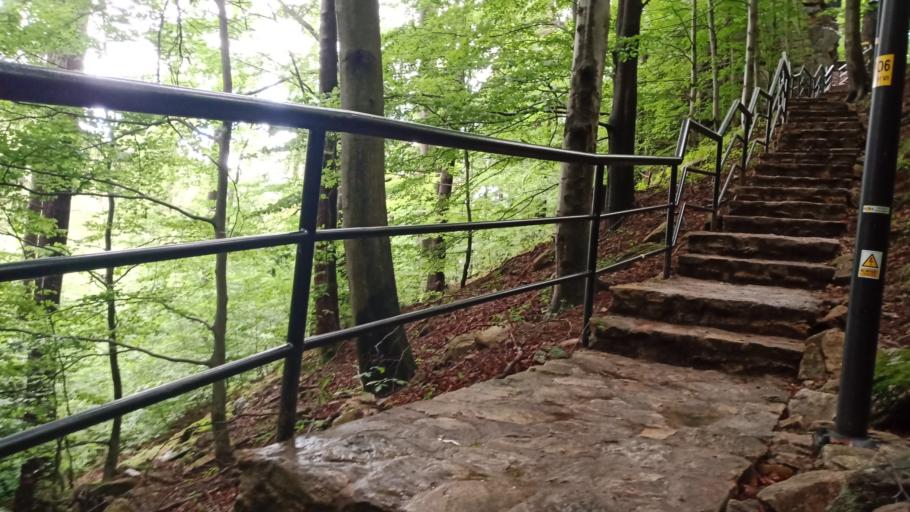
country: PL
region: Lower Silesian Voivodeship
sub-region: Powiat klodzki
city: Miedzylesie
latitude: 50.2308
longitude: 16.7603
